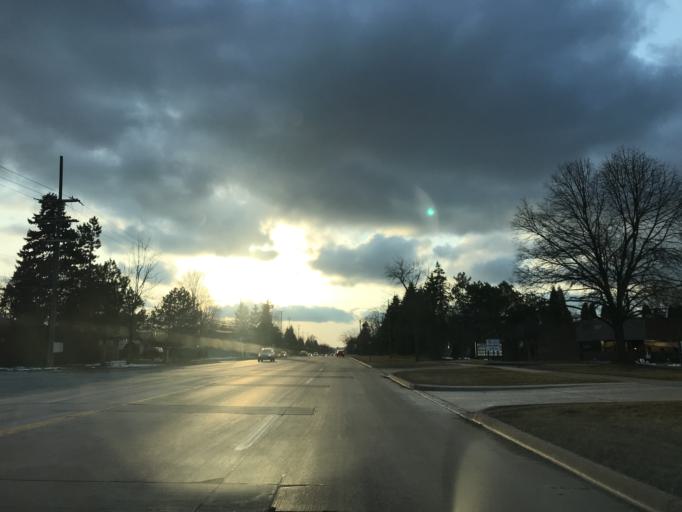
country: US
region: Michigan
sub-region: Oakland County
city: Farmington
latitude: 42.4261
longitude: -83.3799
